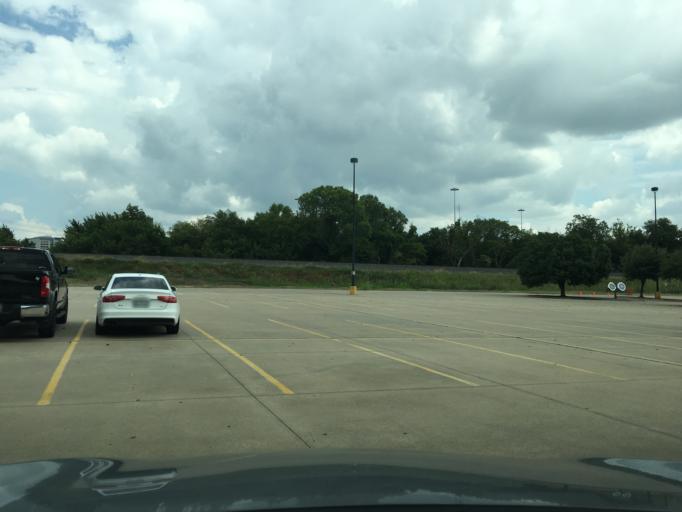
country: US
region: Texas
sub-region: Collin County
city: Plano
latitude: 33.0072
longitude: -96.7100
